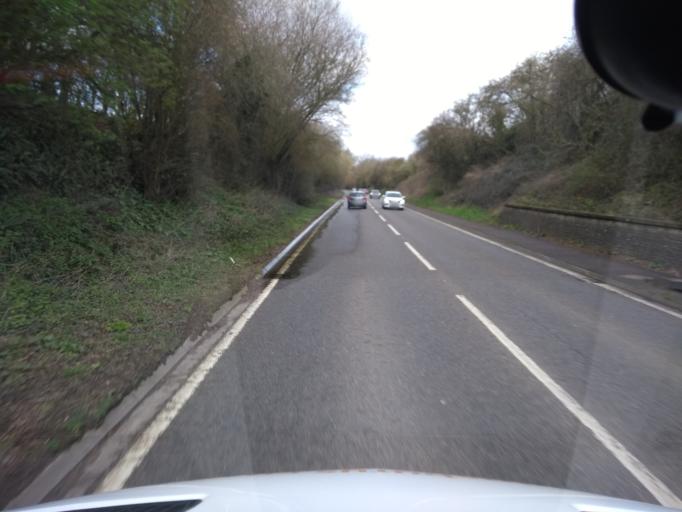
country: GB
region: England
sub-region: Somerset
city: Yeovil
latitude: 50.9451
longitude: -2.6876
